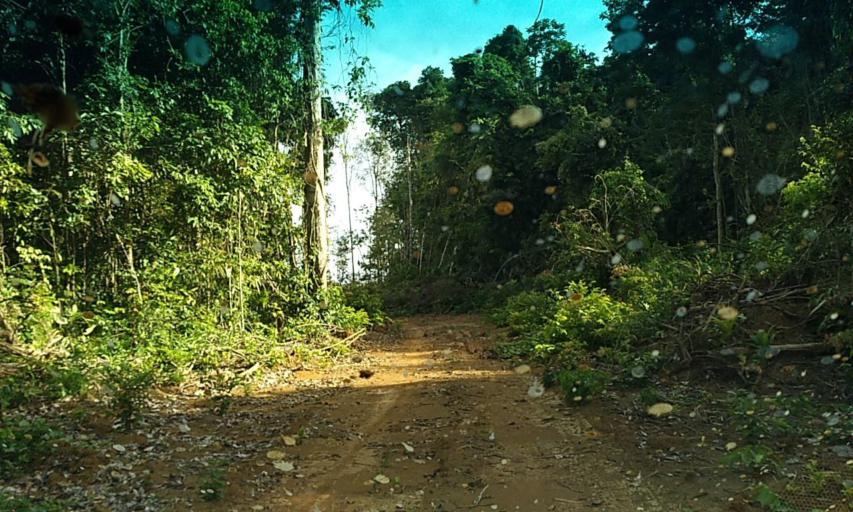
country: BR
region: Para
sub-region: Senador Jose Porfirio
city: Senador Jose Porfirio
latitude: -2.9963
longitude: -51.7429
